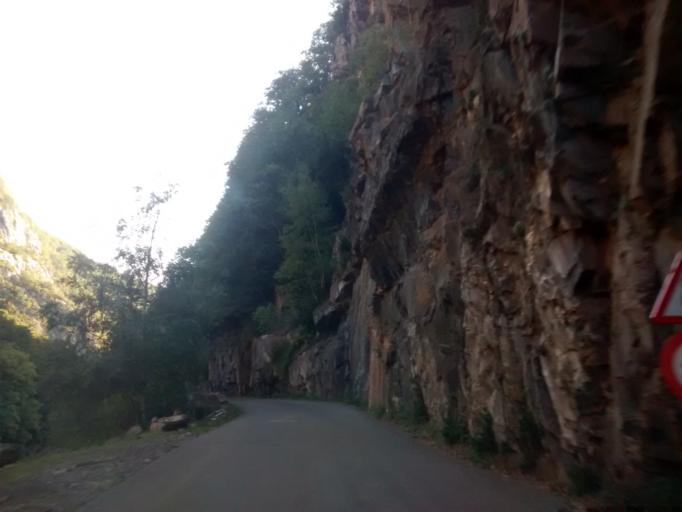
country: ES
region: Aragon
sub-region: Provincia de Huesca
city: Aragues del Puerto
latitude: 42.8081
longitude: -0.7132
